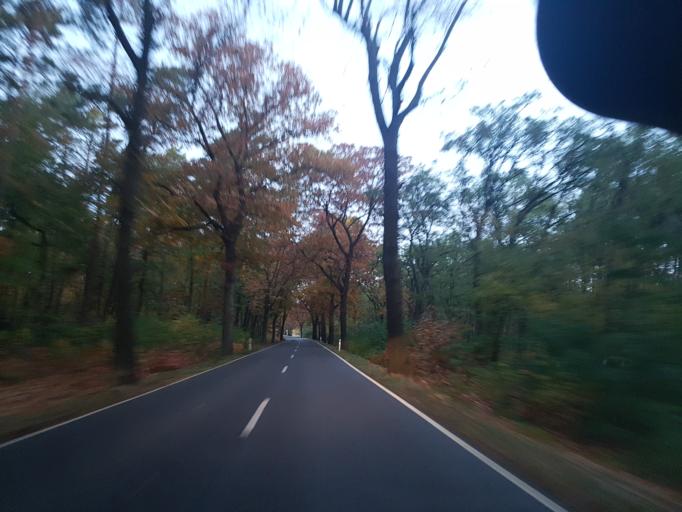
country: DE
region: Brandenburg
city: Ludwigsfelde
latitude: 52.2702
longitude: 13.2218
